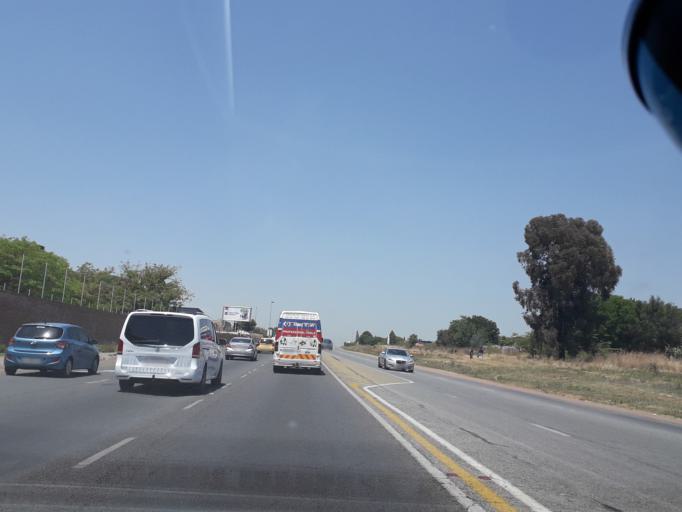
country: ZA
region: Gauteng
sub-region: City of Tshwane Metropolitan Municipality
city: Centurion
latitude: -25.8982
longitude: 28.1595
